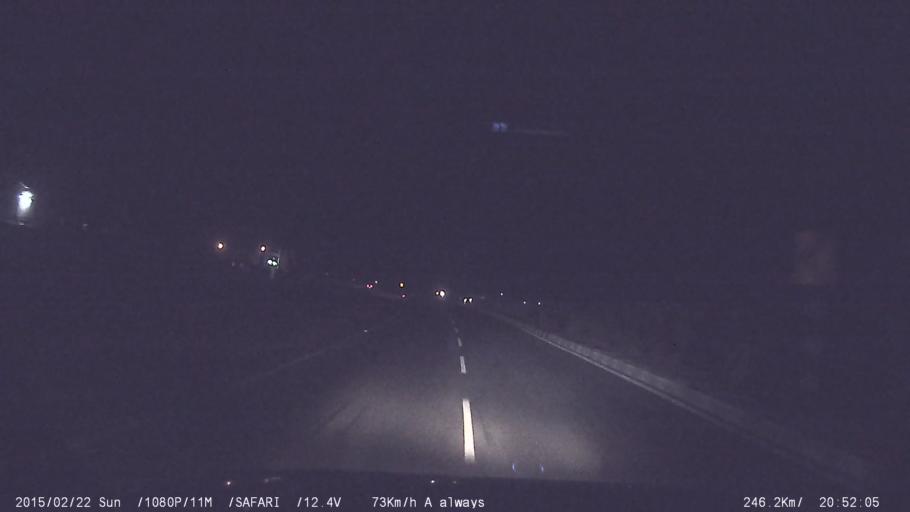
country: IN
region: Tamil Nadu
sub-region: Dindigul
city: Vedasandur
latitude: 10.5486
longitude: 77.9467
